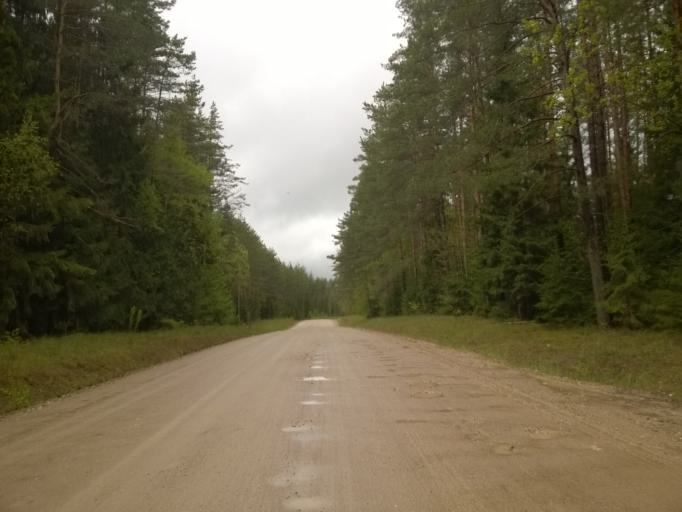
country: LV
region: Amatas Novads
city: Drabesi
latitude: 57.2137
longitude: 25.2334
